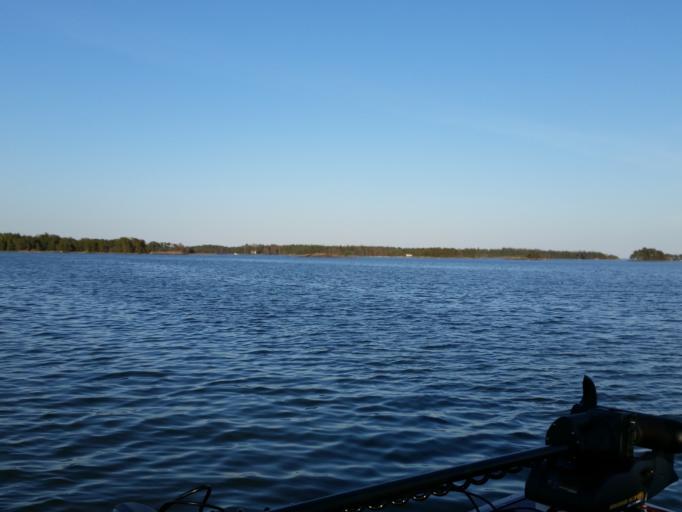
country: FI
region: Uusimaa
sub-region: Helsinki
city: Koukkuniemi
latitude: 60.1364
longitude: 24.7336
